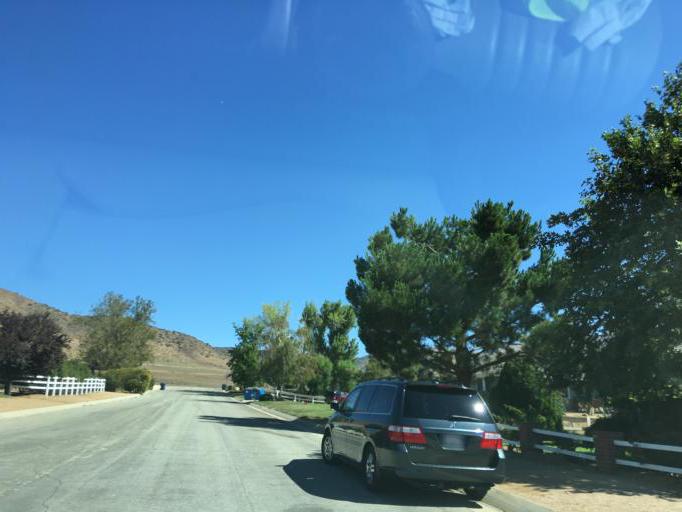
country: US
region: California
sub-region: Los Angeles County
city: Acton
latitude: 34.5047
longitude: -118.1962
